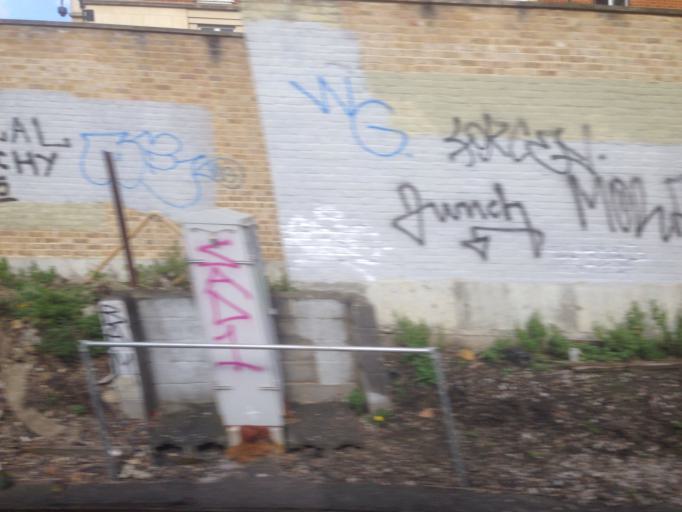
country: GB
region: England
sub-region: Greater London
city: Chelsea
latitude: 51.4807
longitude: -0.1881
